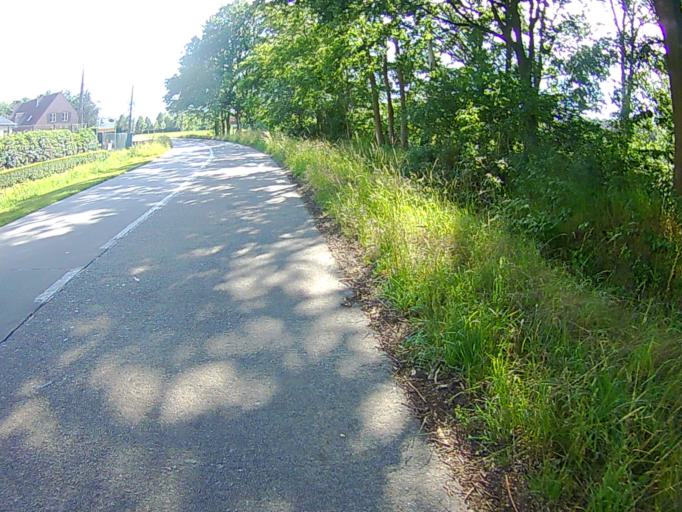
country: BE
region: Flanders
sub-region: Provincie Antwerpen
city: Berlaar
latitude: 51.1283
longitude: 4.6662
